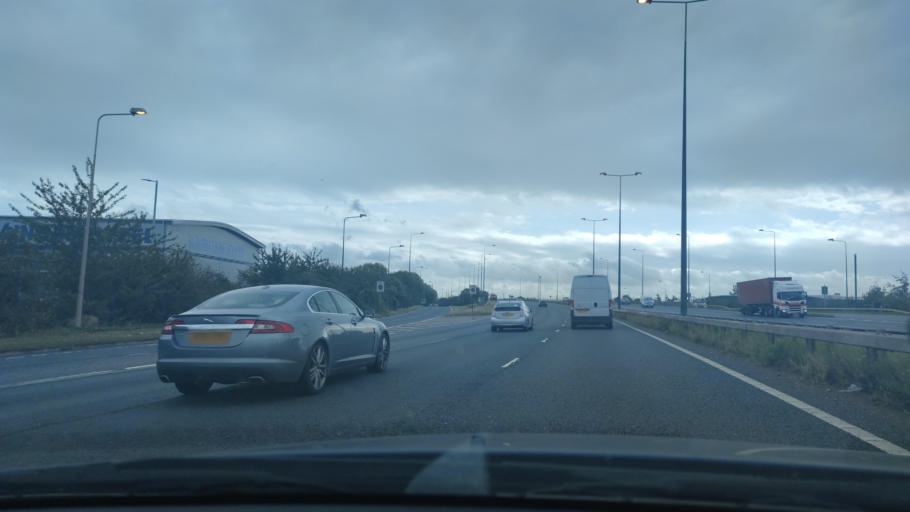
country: GB
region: England
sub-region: Greater London
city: Erith
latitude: 51.5139
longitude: 0.1799
